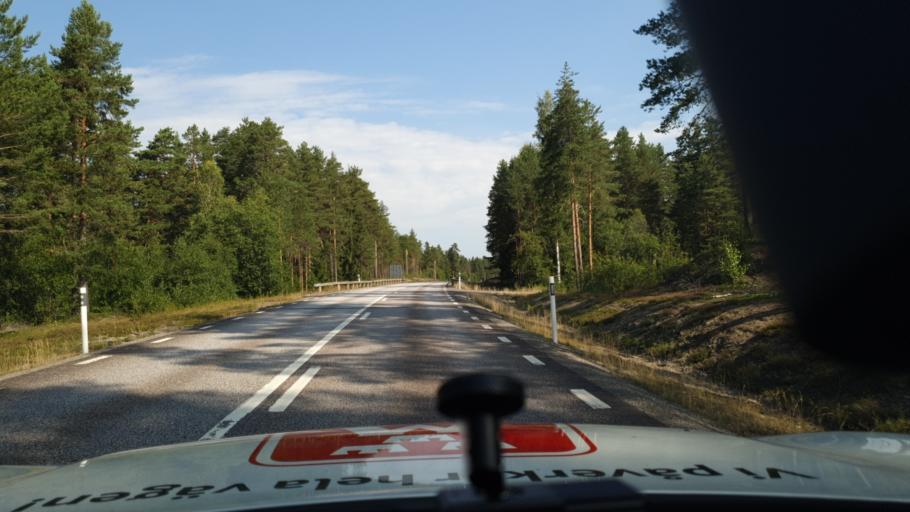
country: SE
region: Vaermland
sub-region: Hagfors Kommun
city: Ekshaerad
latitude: 60.4307
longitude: 13.2560
